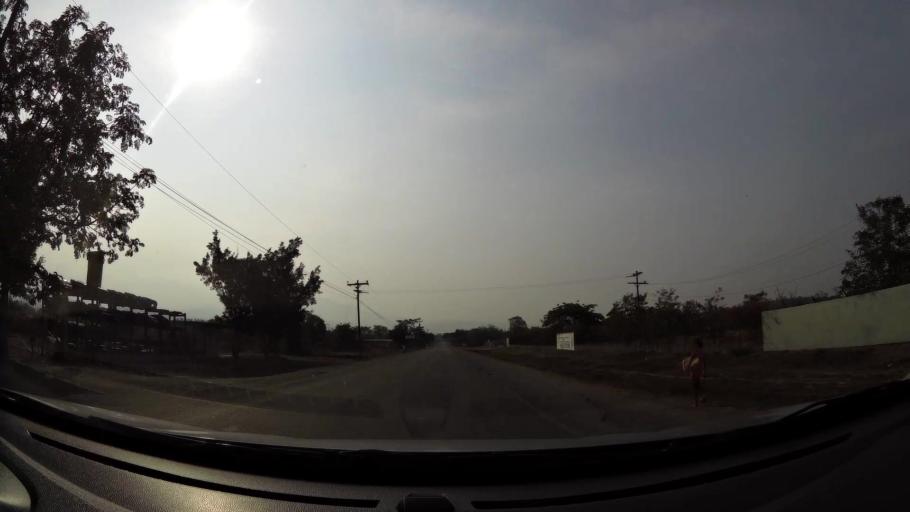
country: HN
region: Comayagua
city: Comayagua
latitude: 14.4610
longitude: -87.6654
